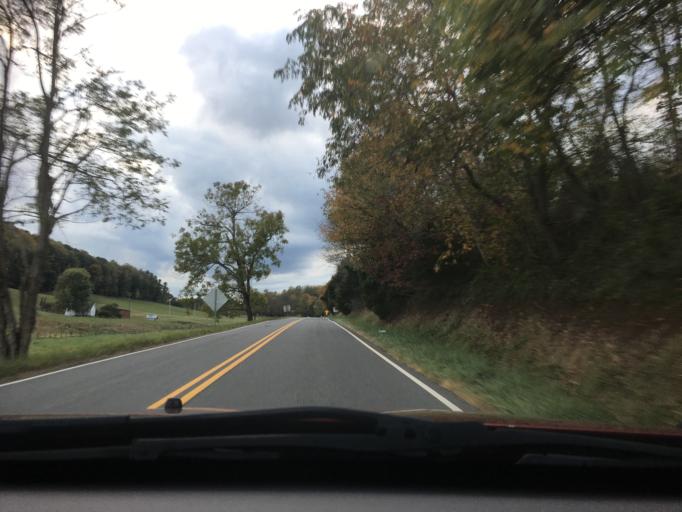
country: US
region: Virginia
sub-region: Giles County
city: Pearisburg
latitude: 37.2172
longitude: -80.7409
